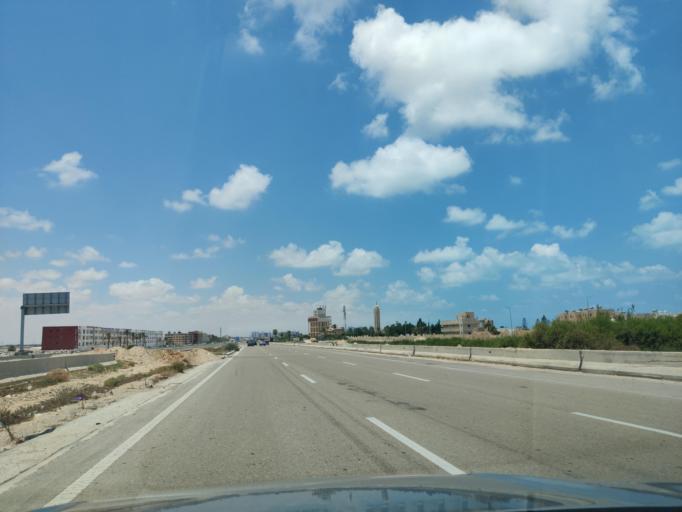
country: EG
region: Muhafazat Matruh
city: Al `Alamayn
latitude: 30.8159
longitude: 29.0358
